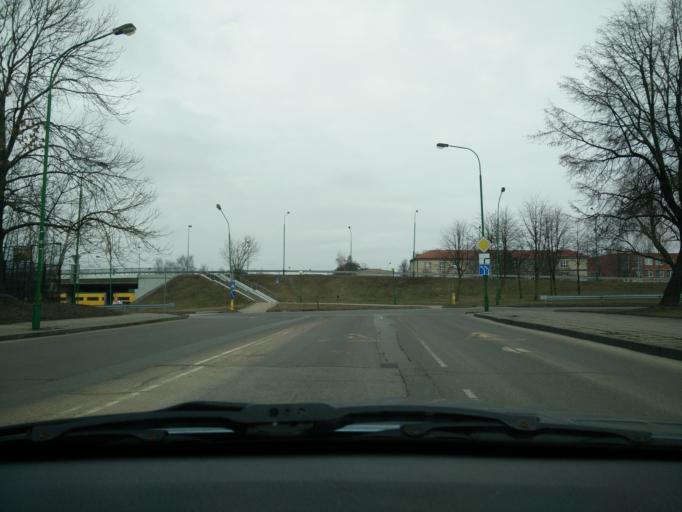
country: LT
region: Klaipedos apskritis
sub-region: Klaipeda
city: Klaipeda
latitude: 55.7110
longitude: 21.1477
